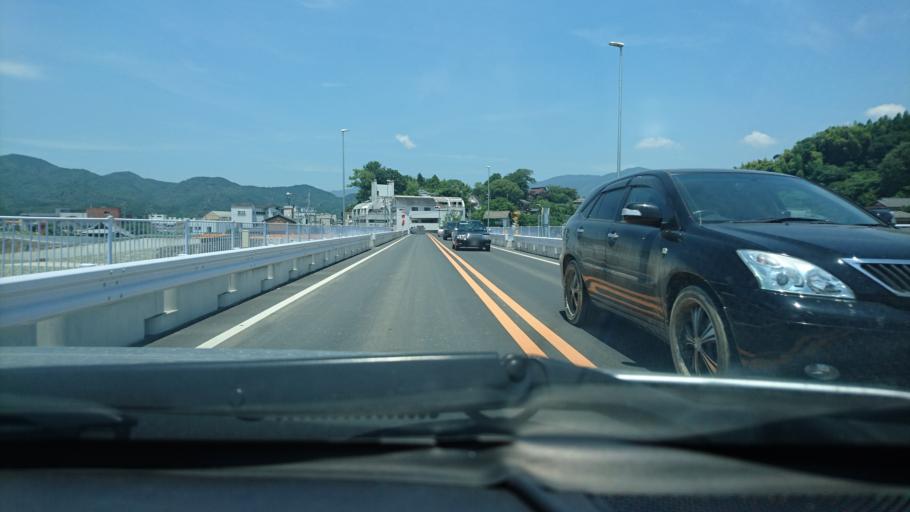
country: JP
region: Ehime
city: Ozu
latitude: 33.5086
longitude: 132.5455
